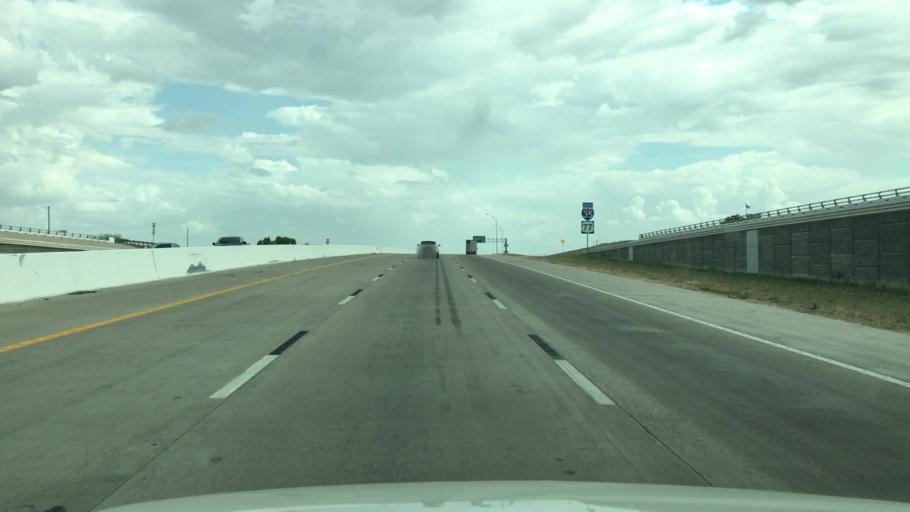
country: US
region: Texas
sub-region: McLennan County
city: West
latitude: 31.7870
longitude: -97.1028
